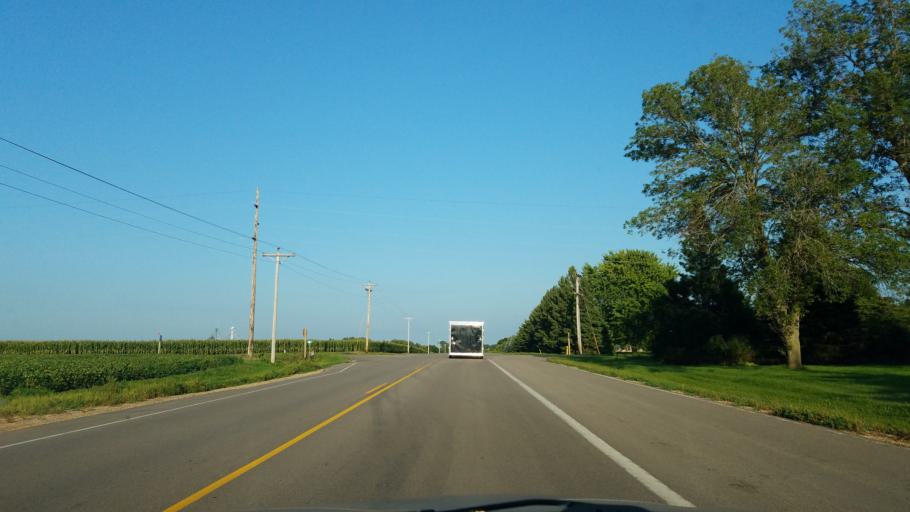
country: US
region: Wisconsin
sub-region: Saint Croix County
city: New Richmond
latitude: 45.0790
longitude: -92.5181
